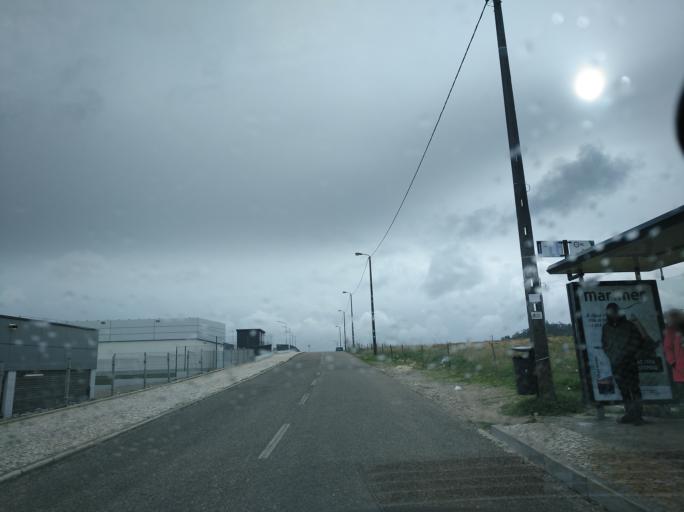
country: PT
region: Lisbon
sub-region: Odivelas
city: Canecas
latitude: 38.7980
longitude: -9.2299
